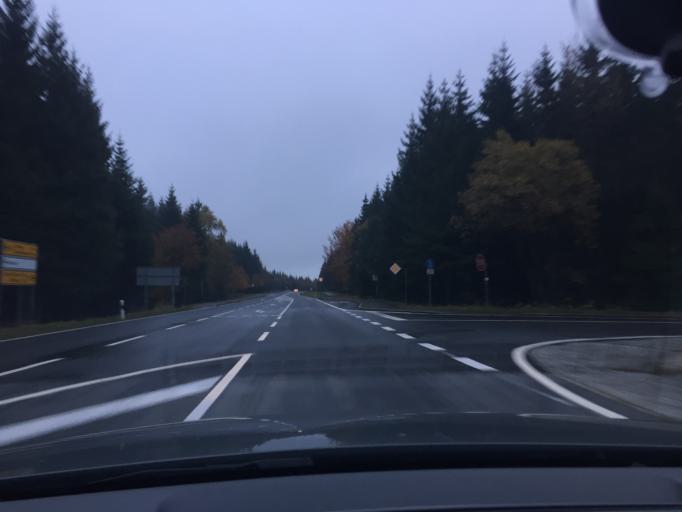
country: DE
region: Saxony
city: Altenberg
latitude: 50.7696
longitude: 13.7331
